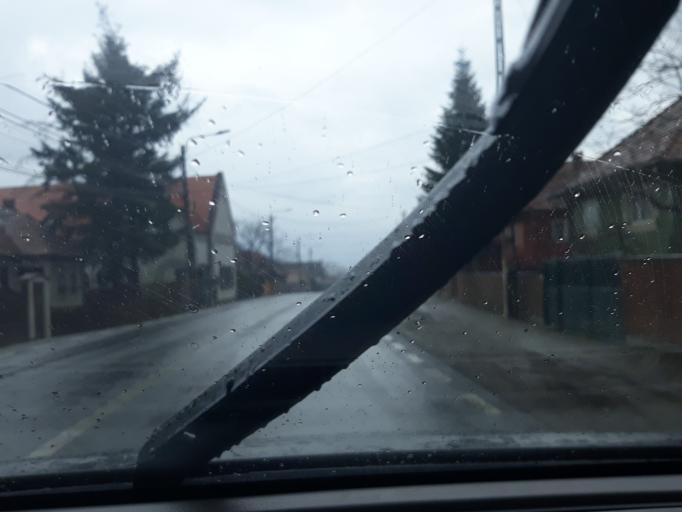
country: RO
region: Harghita
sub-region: Comuna Corund
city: Corund
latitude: 46.4743
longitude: 25.1781
